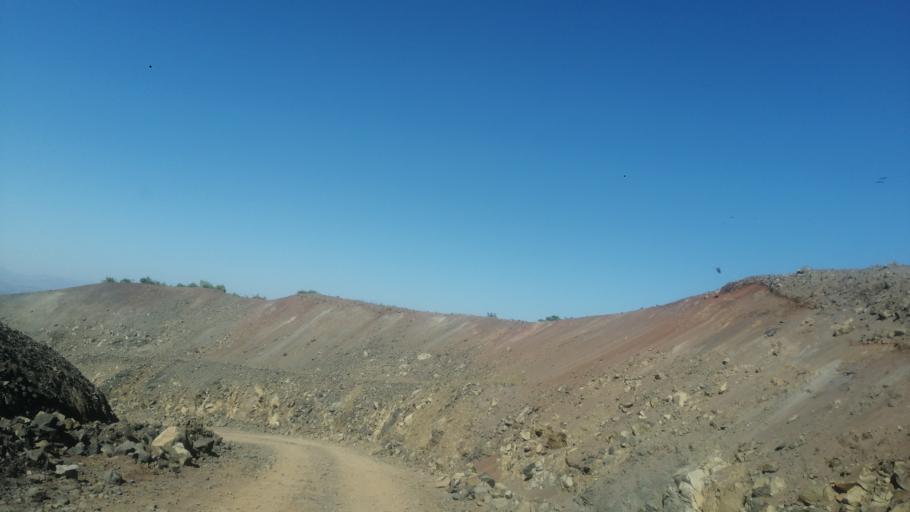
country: ET
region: Amhara
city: Addiet Canna
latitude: 11.1532
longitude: 37.8528
